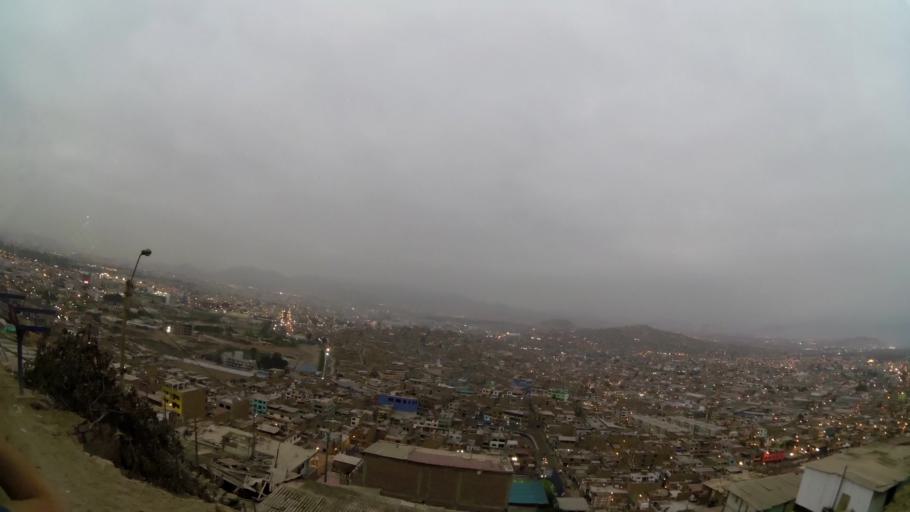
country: PE
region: Lima
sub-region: Lima
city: Surco
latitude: -12.1887
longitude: -77.0206
